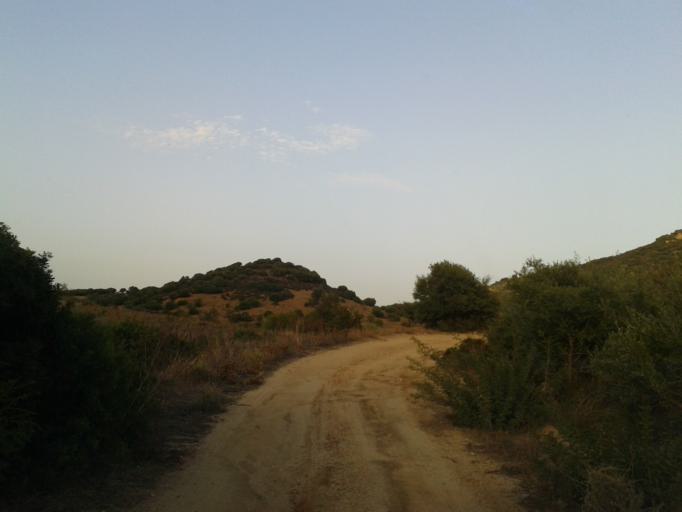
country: IT
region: Sardinia
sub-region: Provincia di Cagliari
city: Villasimius
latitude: 39.1381
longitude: 9.4992
